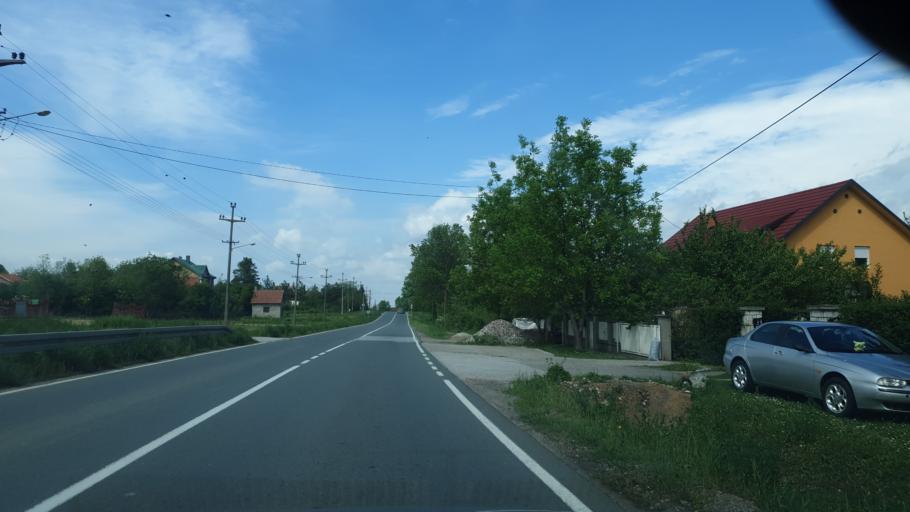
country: RS
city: Stubline
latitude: 44.5959
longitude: 20.1454
